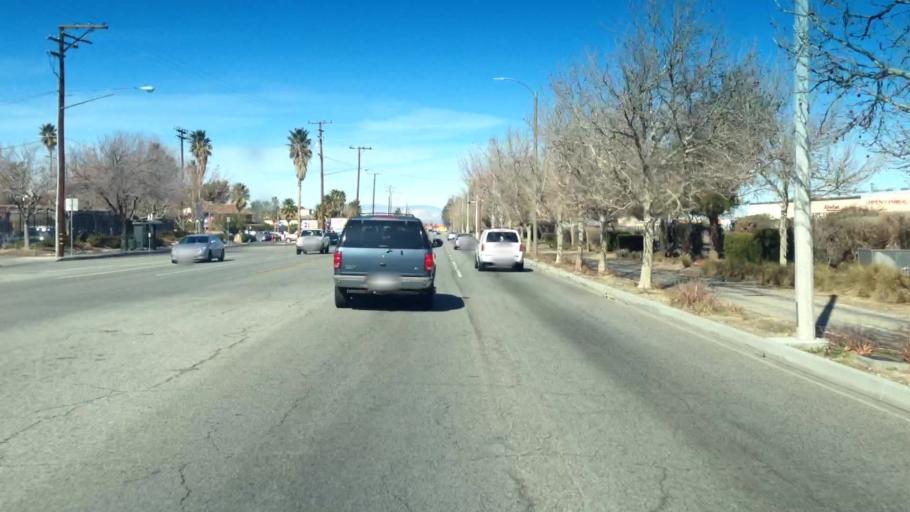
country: US
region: California
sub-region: Los Angeles County
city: Lancaster
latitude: 34.6825
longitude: -118.1341
